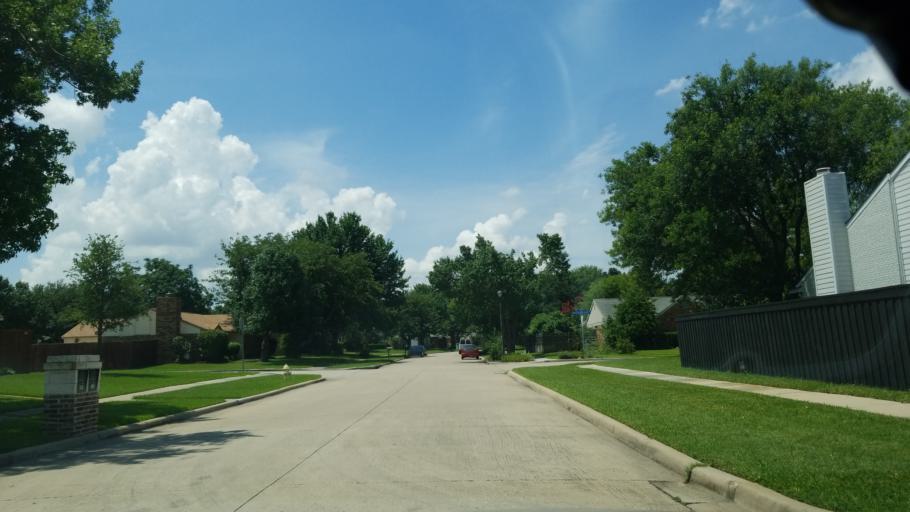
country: US
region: Texas
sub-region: Dallas County
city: Coppell
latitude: 32.9655
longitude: -96.9643
